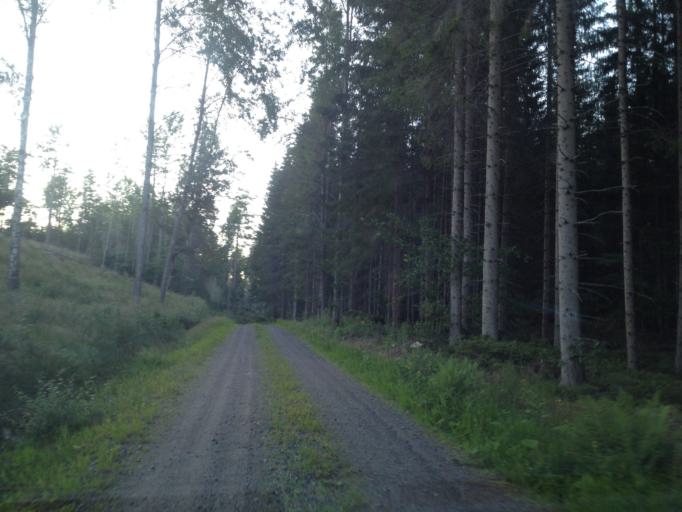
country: SE
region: Kalmar
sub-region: Vasterviks Kommun
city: Overum
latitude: 58.0156
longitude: 16.1194
